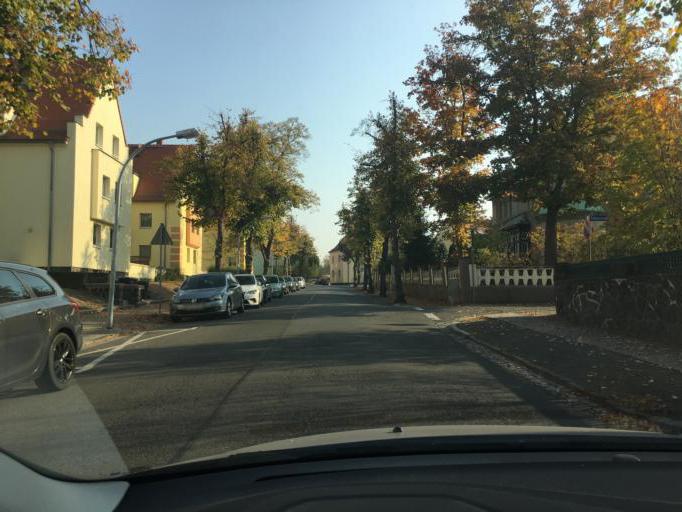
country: DE
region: Saxony
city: Wurzen
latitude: 51.3634
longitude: 12.7360
